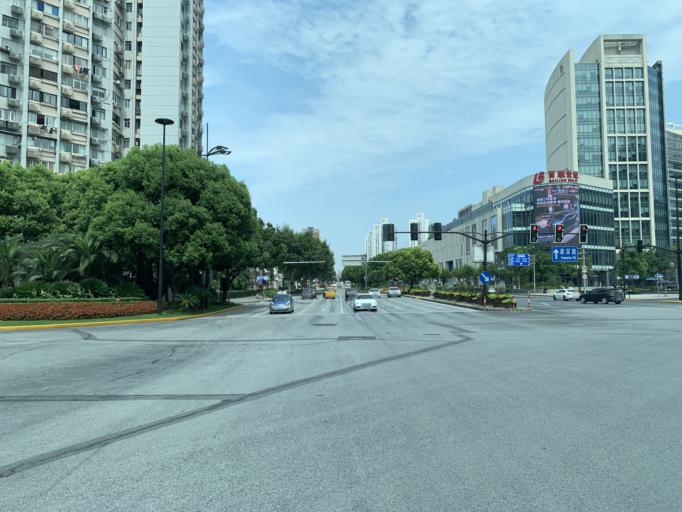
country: CN
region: Shanghai Shi
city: Pudong
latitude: 31.2321
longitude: 121.5205
